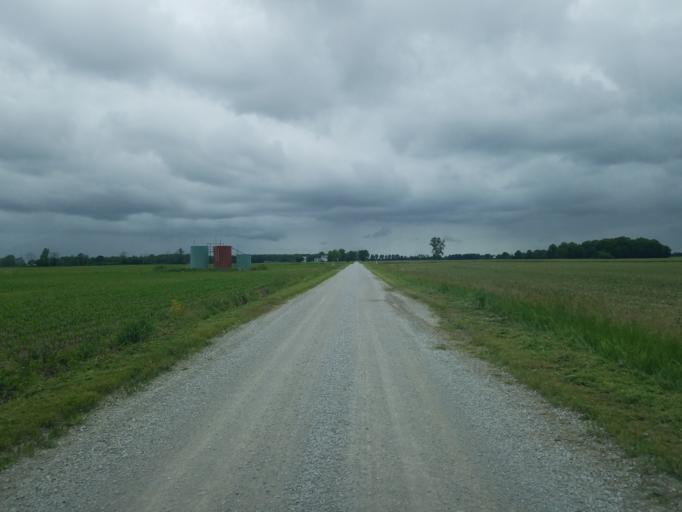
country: US
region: Ohio
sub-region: Morrow County
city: Cardington
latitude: 40.5338
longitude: -82.9340
